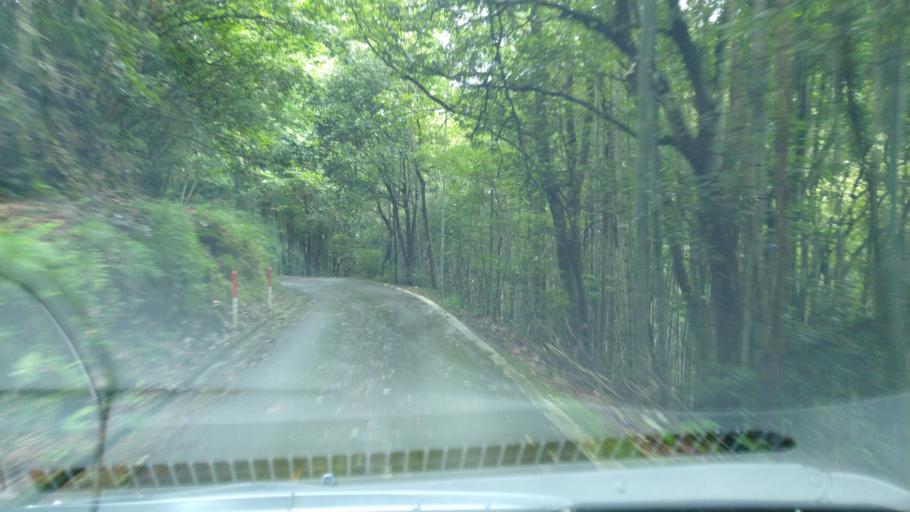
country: JP
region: Kyoto
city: Ayabe
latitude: 35.2395
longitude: 135.2634
